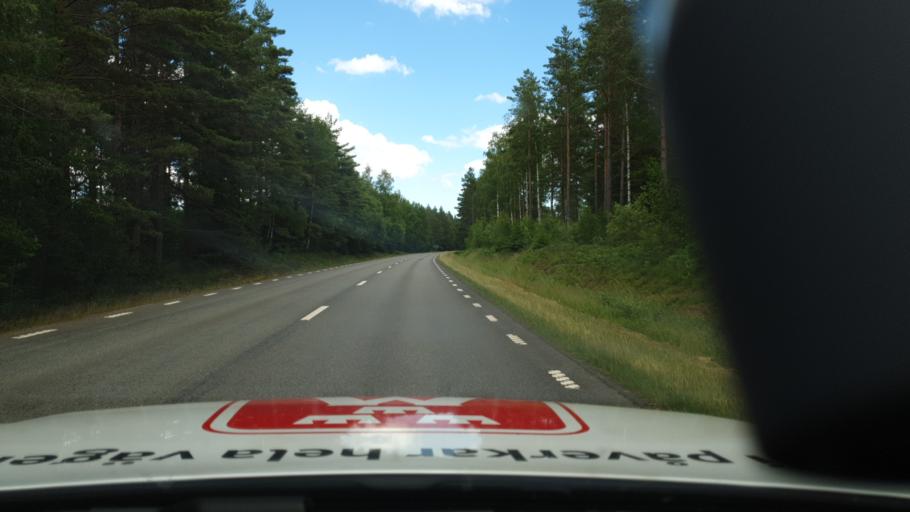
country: SE
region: Vaestra Goetaland
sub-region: Karlsborgs Kommun
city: Molltorp
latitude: 58.4076
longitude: 14.3655
